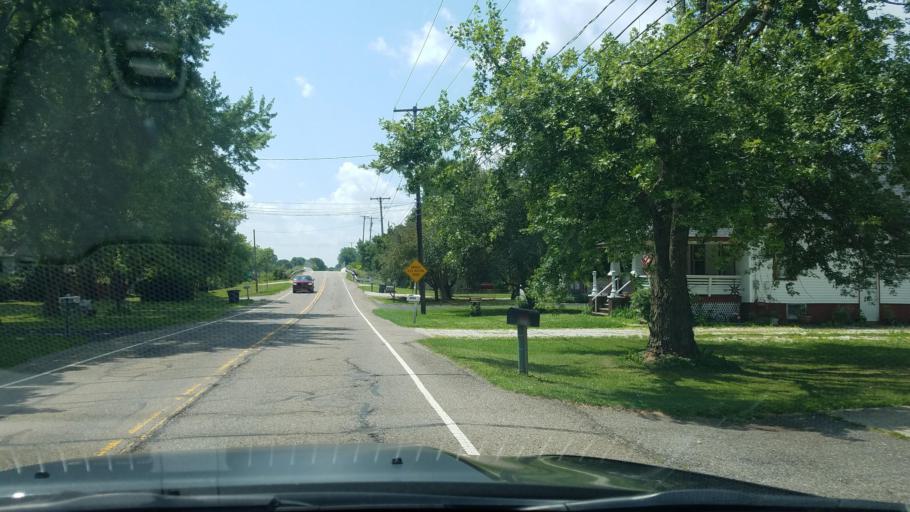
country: US
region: Ohio
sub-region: Trumbull County
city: Leavittsburg
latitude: 41.2710
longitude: -80.8677
